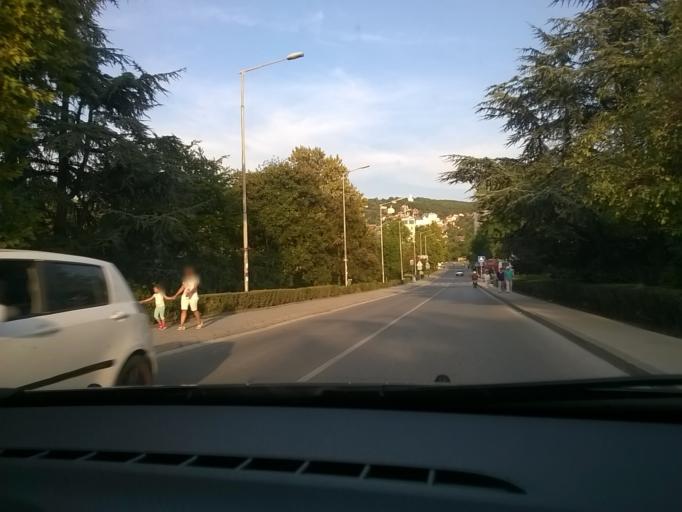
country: RS
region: Autonomna Pokrajina Vojvodina
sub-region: Juznobanatski Okrug
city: Vrsac
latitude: 45.1175
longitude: 21.3062
